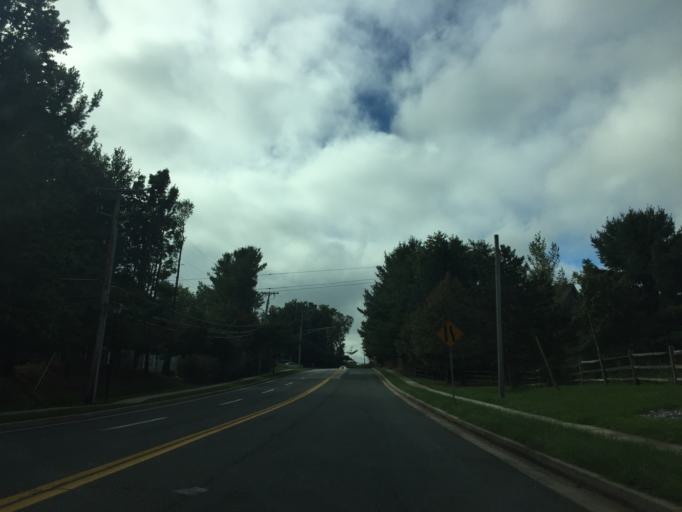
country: US
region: Maryland
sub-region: Baltimore County
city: Pikesville
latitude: 39.3823
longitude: -76.6741
